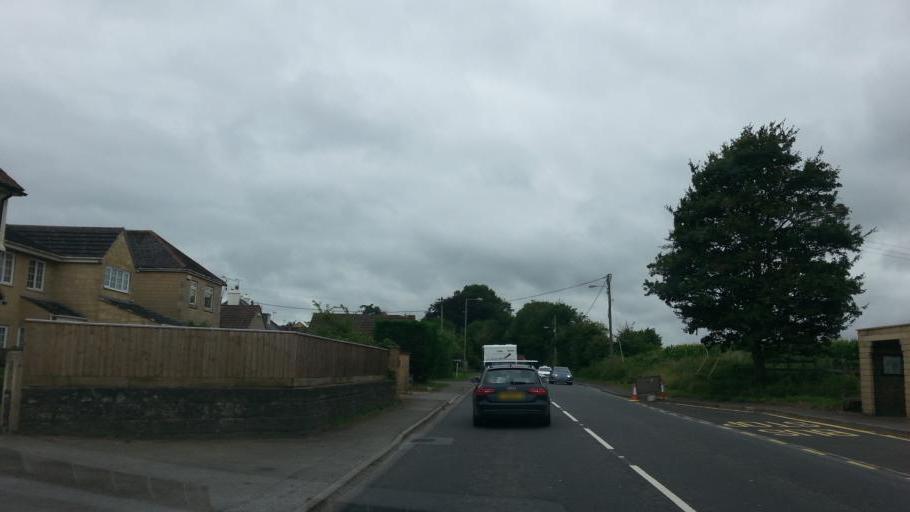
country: GB
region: England
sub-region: Wiltshire
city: Lacock
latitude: 51.3976
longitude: -2.1336
